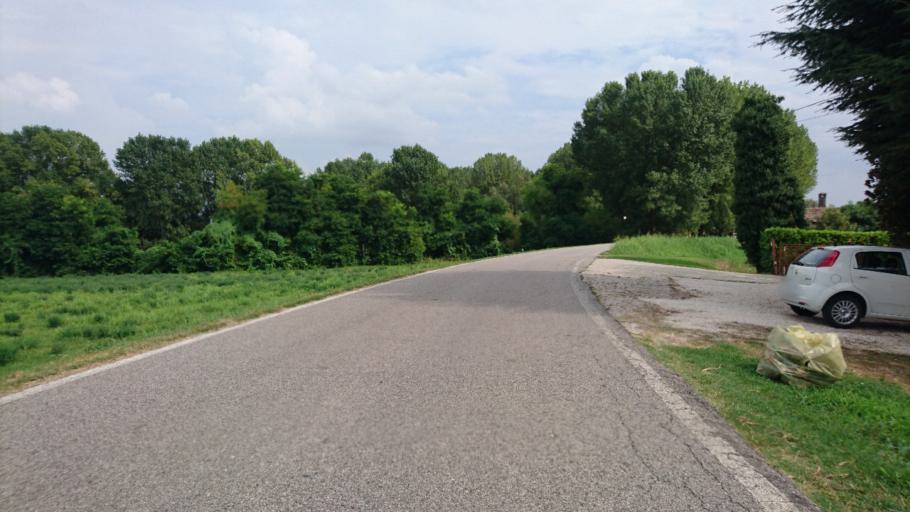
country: IT
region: Veneto
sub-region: Provincia di Padova
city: Cervarese Santa Croce
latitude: 45.4164
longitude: 11.7084
